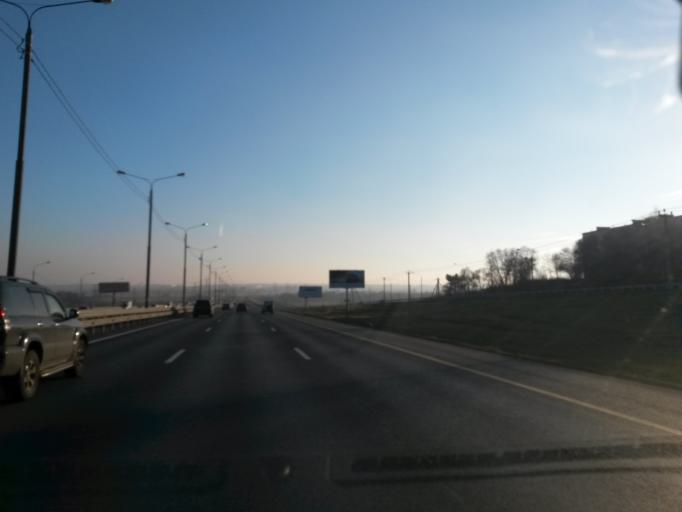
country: RU
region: Moskovskaya
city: Shcherbinka
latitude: 55.4733
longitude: 37.6163
